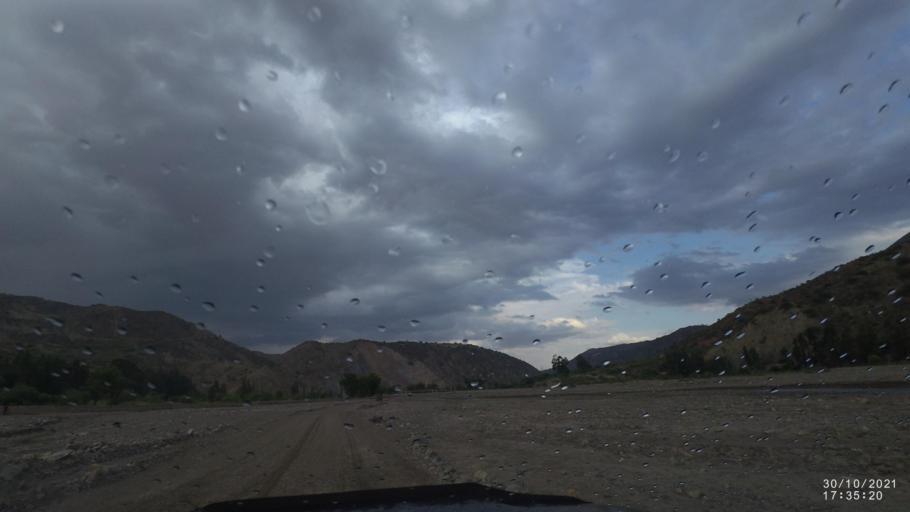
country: BO
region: Cochabamba
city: Sipe Sipe
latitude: -17.5259
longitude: -66.5720
